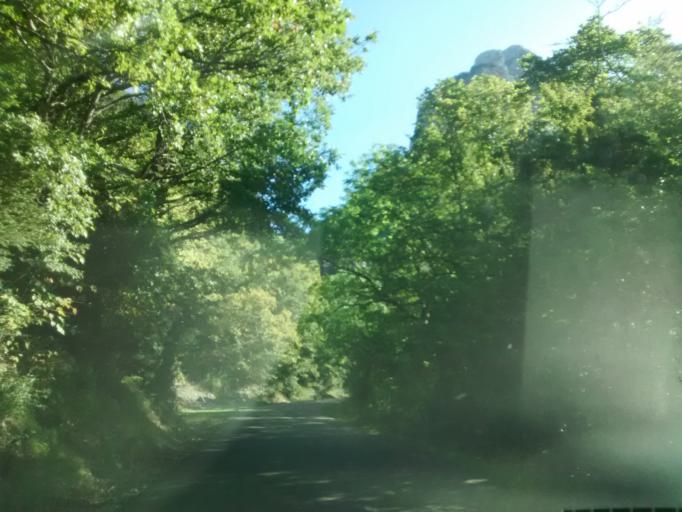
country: ES
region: Aragon
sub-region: Provincia de Huesca
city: Aragues del Puerto
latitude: 42.8004
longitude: -0.7236
